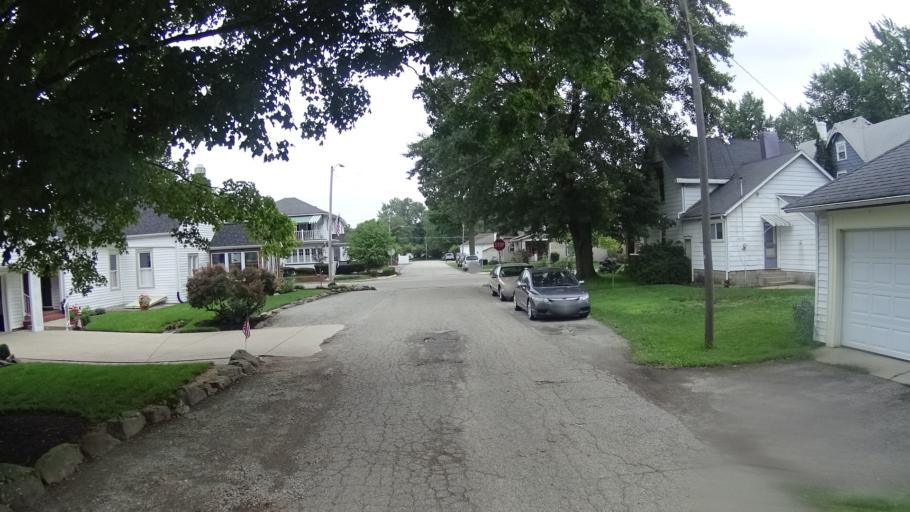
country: US
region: Indiana
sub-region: Madison County
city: Pendleton
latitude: 40.0021
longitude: -85.7435
